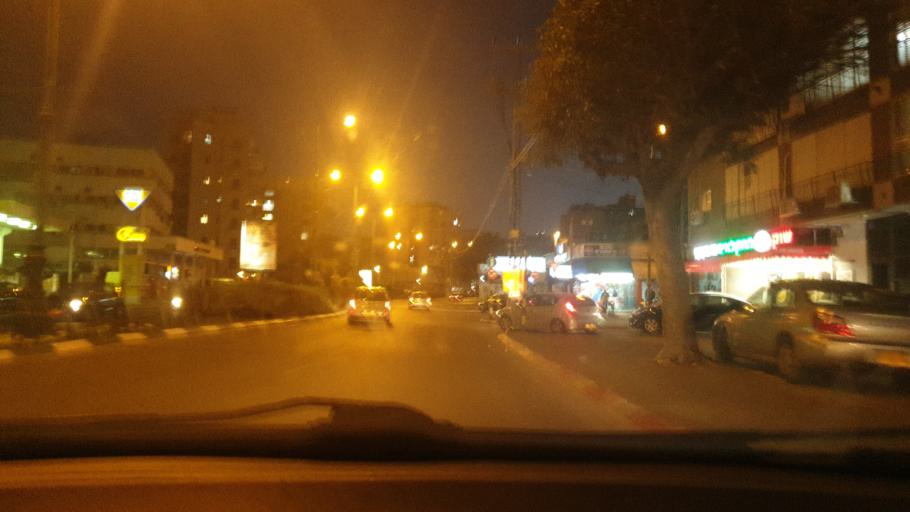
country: IL
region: Central District
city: Rishon LeZiyyon
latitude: 31.9724
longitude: 34.8064
